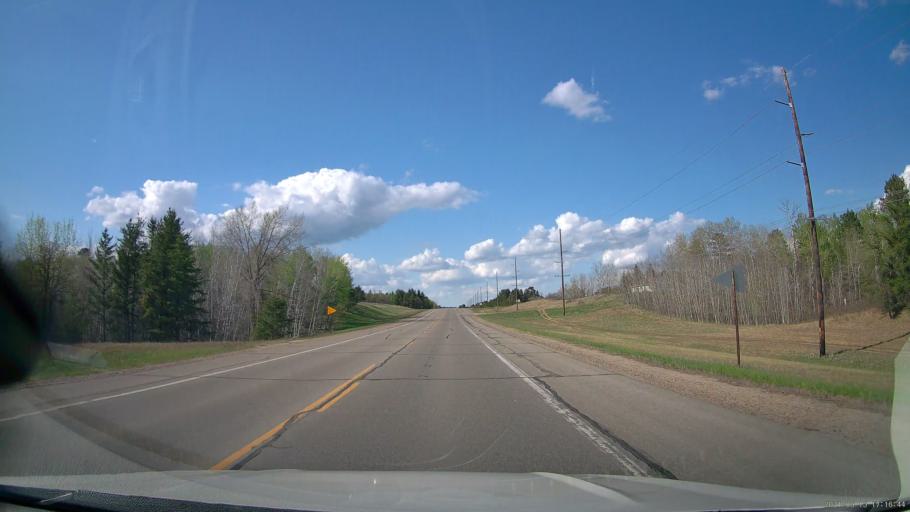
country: US
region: Minnesota
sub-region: Hubbard County
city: Park Rapids
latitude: 46.9332
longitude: -95.0168
